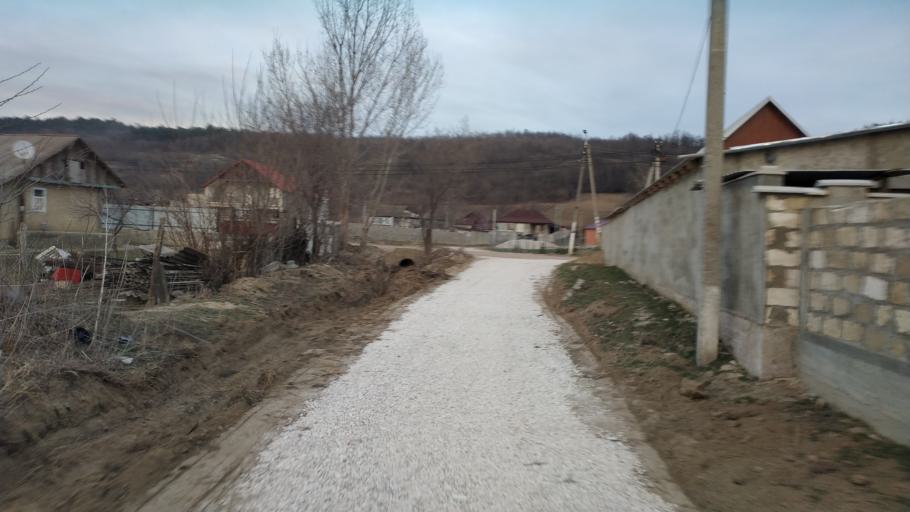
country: MD
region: Hincesti
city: Dancu
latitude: 46.7606
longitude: 28.2084
